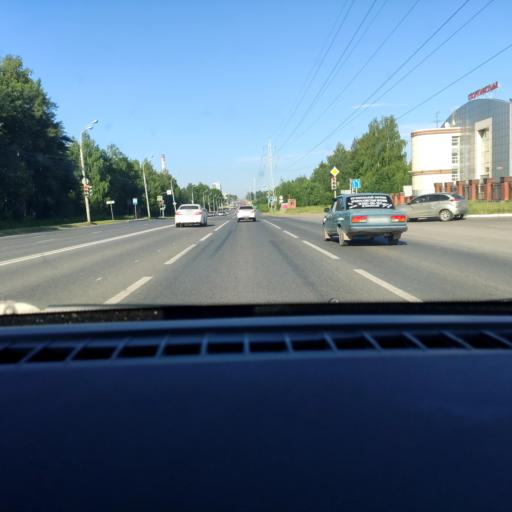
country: RU
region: Udmurtiya
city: Khokhryaki
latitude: 56.8984
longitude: 53.3032
